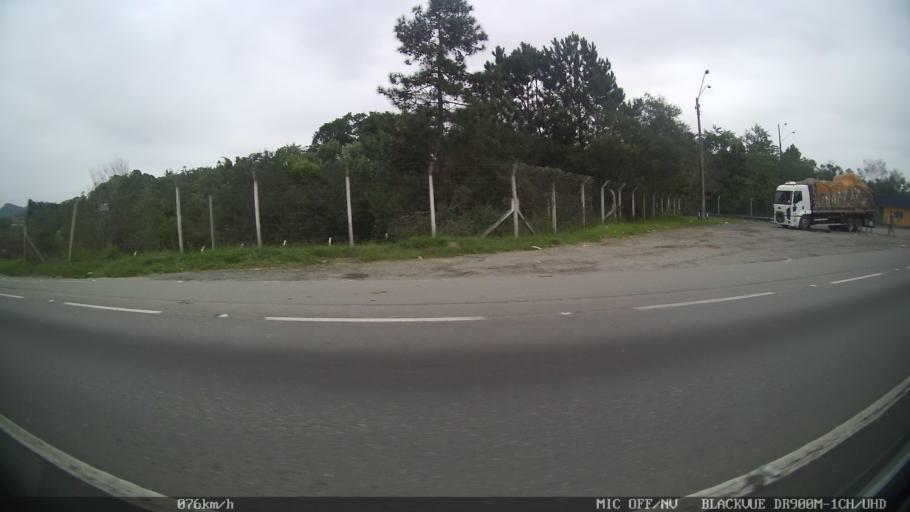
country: BR
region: Santa Catarina
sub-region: Barra Velha
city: Barra Velha
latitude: -26.6118
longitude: -48.7220
